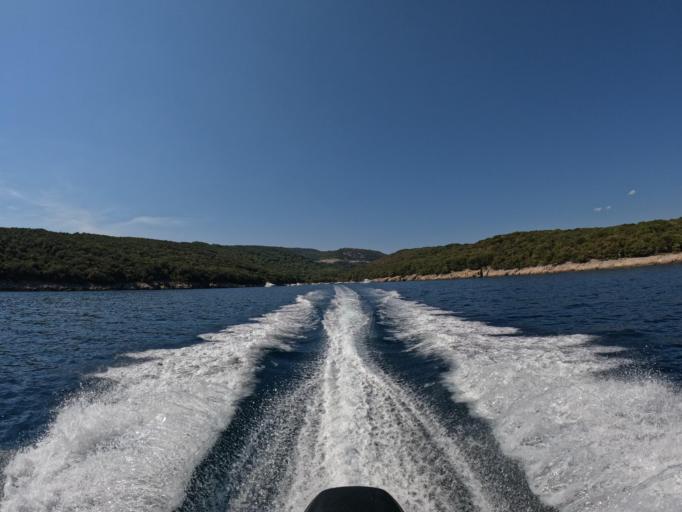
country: HR
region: Primorsko-Goranska
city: Cres
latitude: 44.9480
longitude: 14.4655
